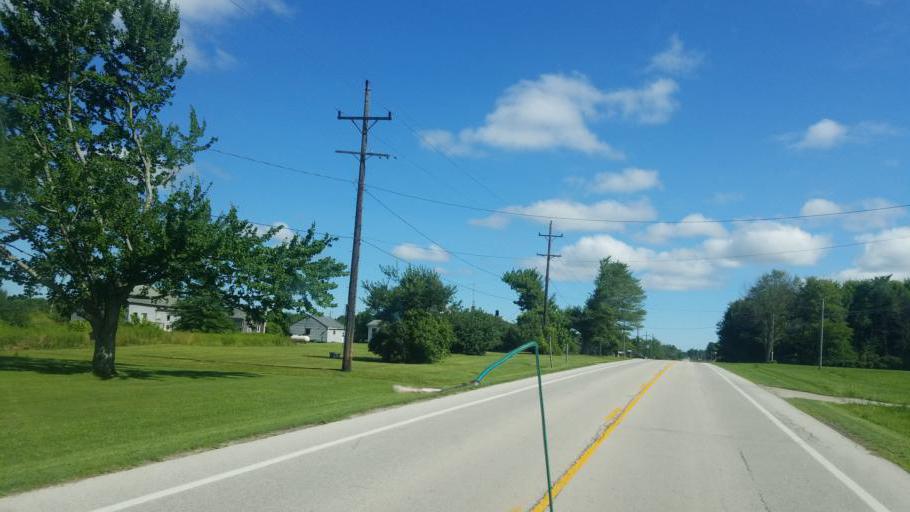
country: US
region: Ohio
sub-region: Ashtabula County
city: Conneaut
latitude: 41.8300
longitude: -80.5722
